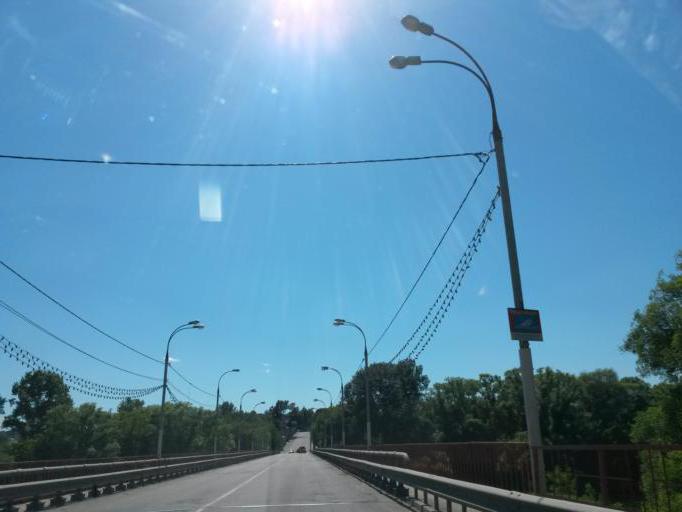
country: RU
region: Moskovskaya
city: Serpukhov
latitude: 54.9159
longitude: 37.4004
